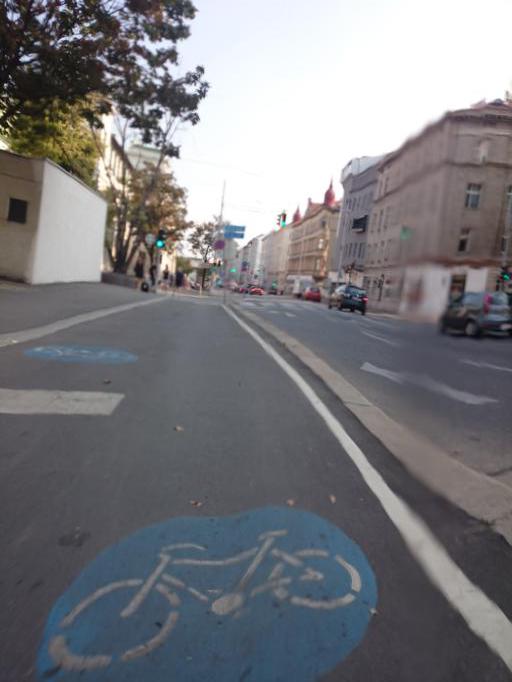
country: AT
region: Vienna
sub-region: Wien Stadt
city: Vienna
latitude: 48.2247
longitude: 16.3497
